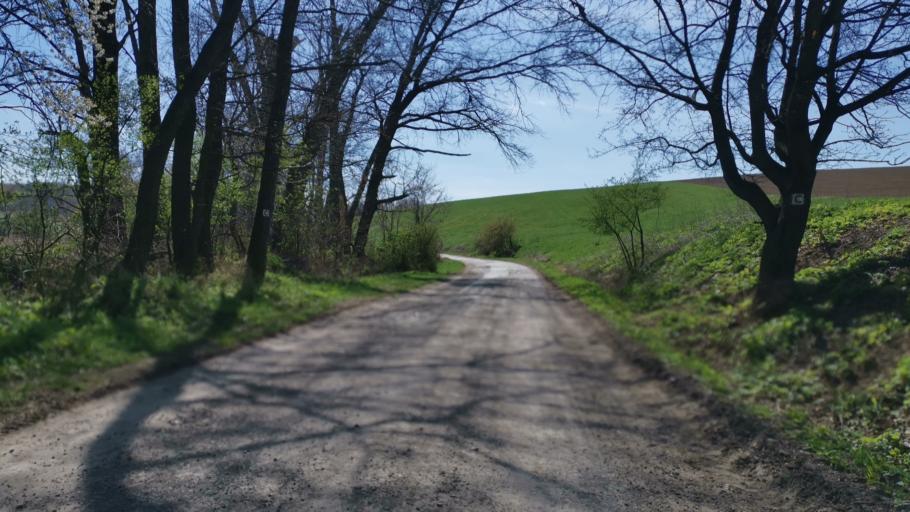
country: SK
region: Trnavsky
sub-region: Okres Senica
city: Senica
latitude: 48.7501
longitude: 17.2839
